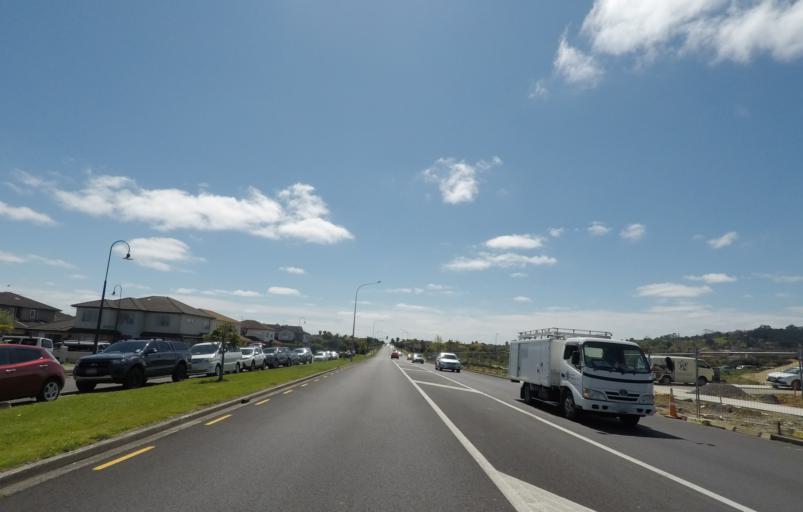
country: NZ
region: Auckland
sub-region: Auckland
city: Manukau City
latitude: -36.9557
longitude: 174.9091
